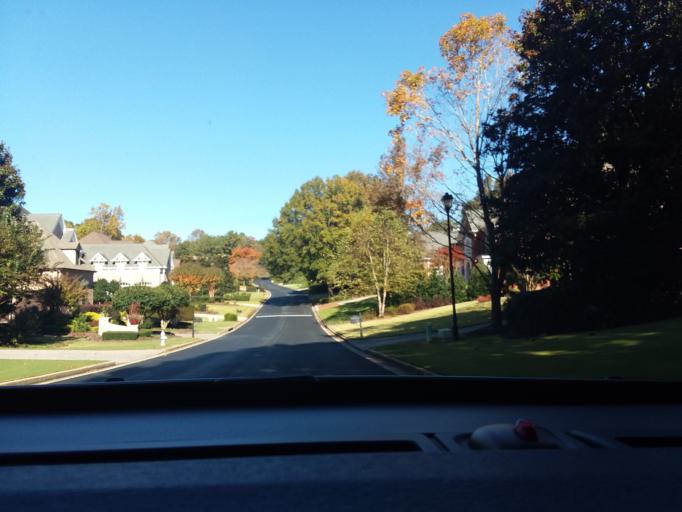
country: US
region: Georgia
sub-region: Fulton County
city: Johns Creek
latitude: 34.0243
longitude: -84.1829
